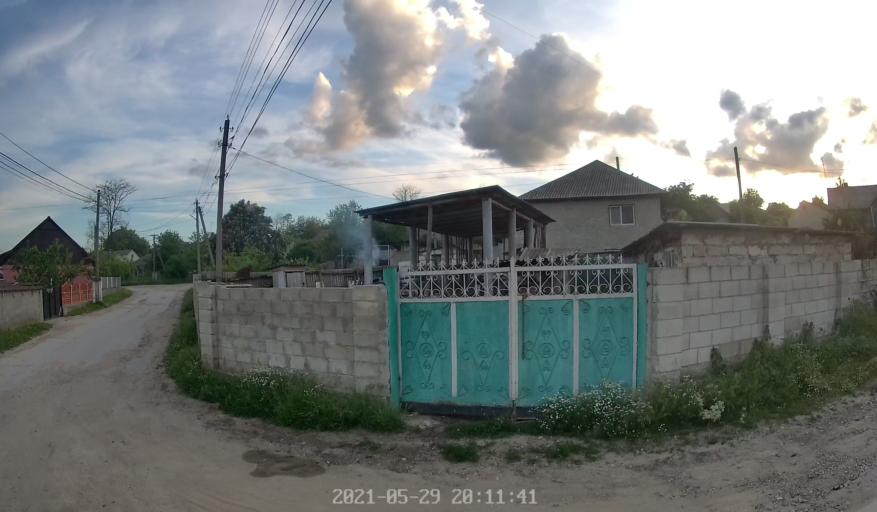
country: MD
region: Chisinau
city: Singera
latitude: 46.8259
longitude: 28.9747
